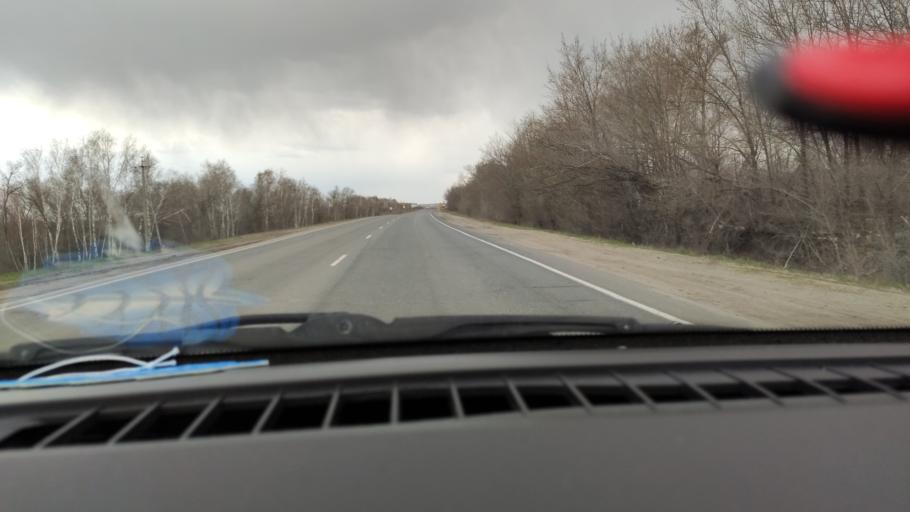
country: RU
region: Saratov
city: Sinodskoye
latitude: 52.0239
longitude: 46.7111
